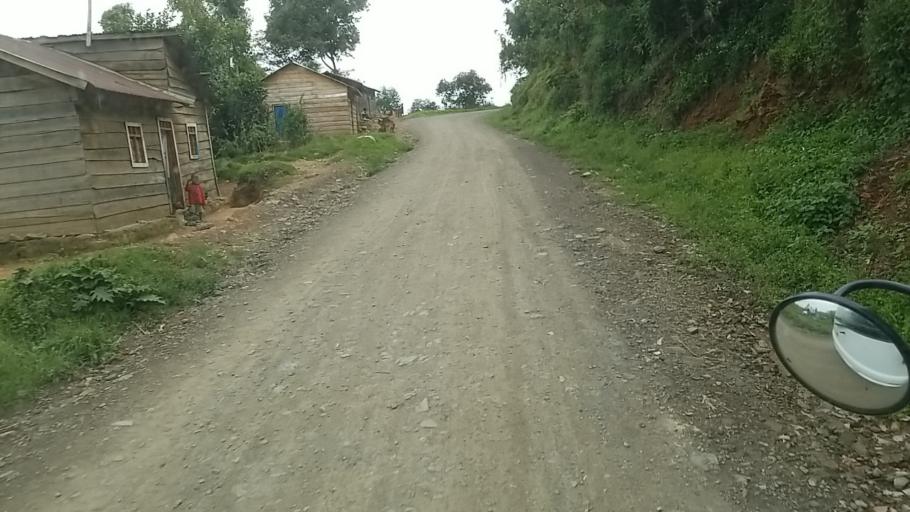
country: CD
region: Nord Kivu
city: Sake
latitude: -1.9225
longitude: 28.9456
